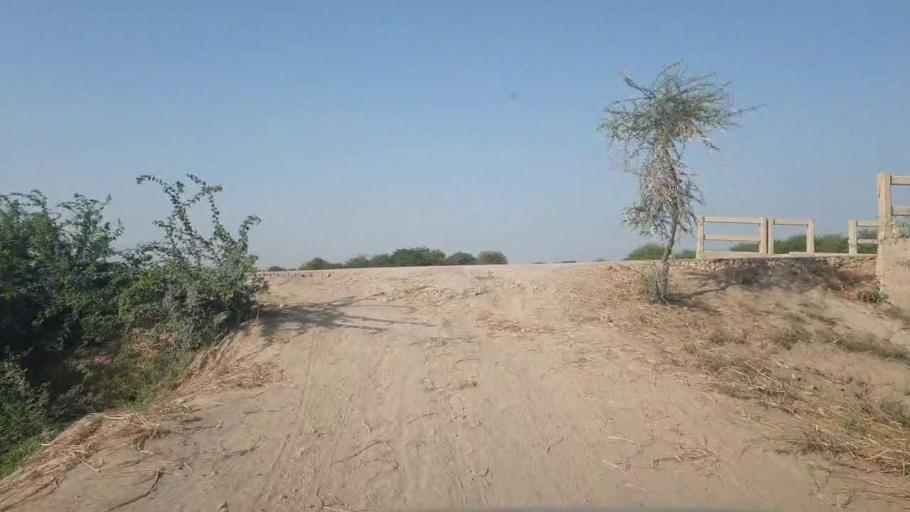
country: PK
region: Sindh
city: Badin
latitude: 24.6393
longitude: 68.8150
